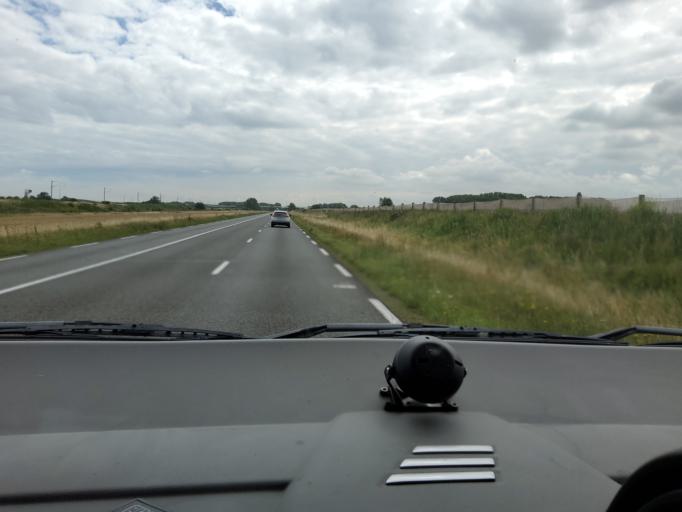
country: FR
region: Nord-Pas-de-Calais
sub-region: Departement du Nord
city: Loon-Plage
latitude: 50.9958
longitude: 2.1809
